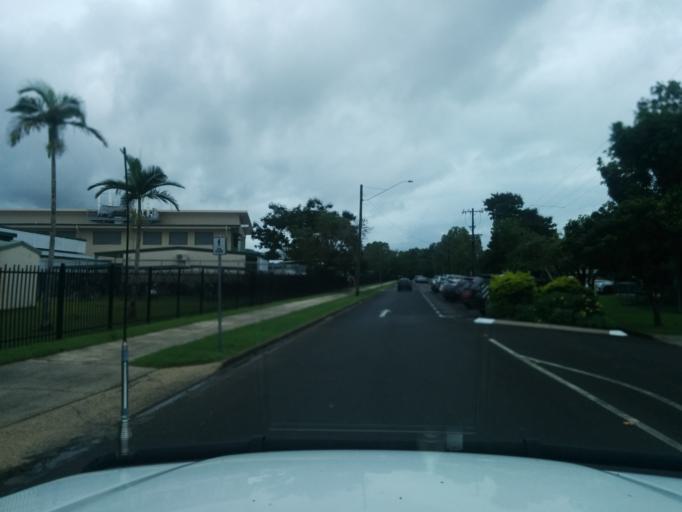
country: AU
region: Queensland
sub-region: Cairns
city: Cairns
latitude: -16.9230
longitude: 145.7535
